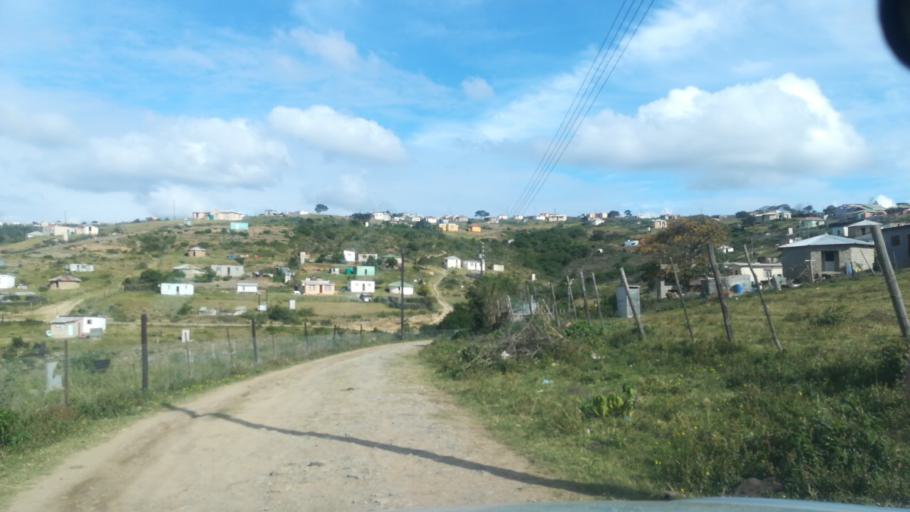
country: ZA
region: Eastern Cape
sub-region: Amathole District Municipality
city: Komga
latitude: -32.7583
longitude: 27.9530
